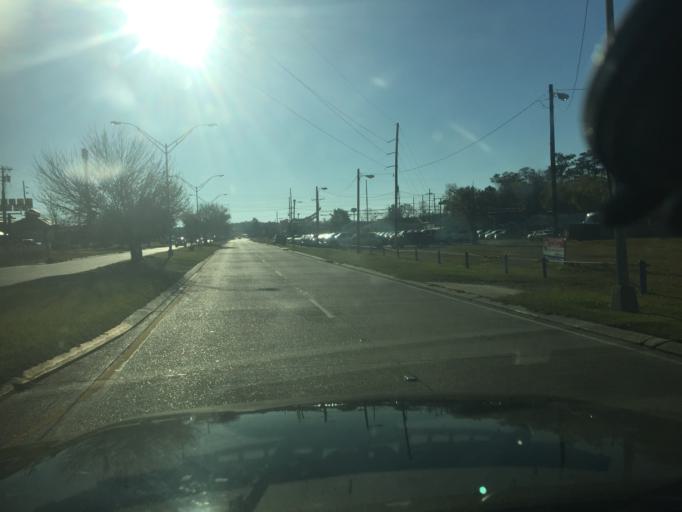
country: US
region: Louisiana
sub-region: Saint Tammany Parish
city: Slidell
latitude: 30.2510
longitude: -89.7667
